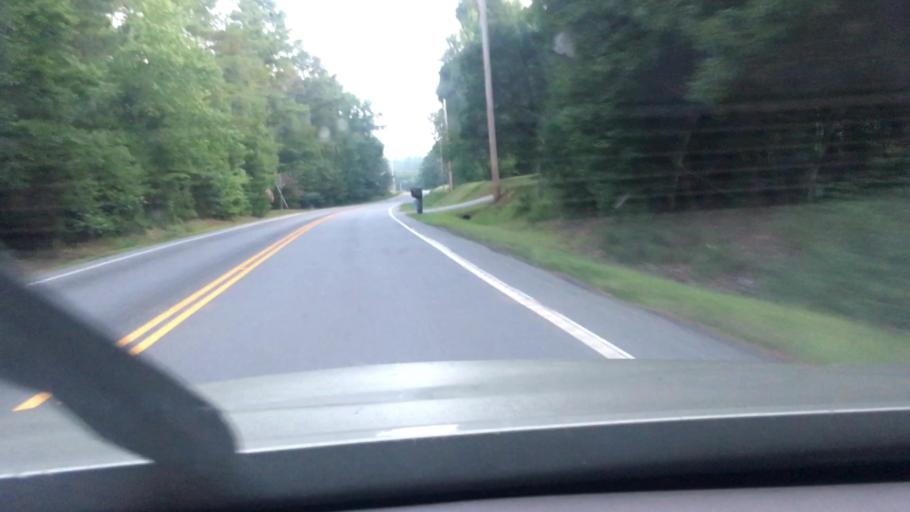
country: US
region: South Carolina
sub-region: Lexington County
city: Irmo
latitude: 34.1426
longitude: -81.1908
